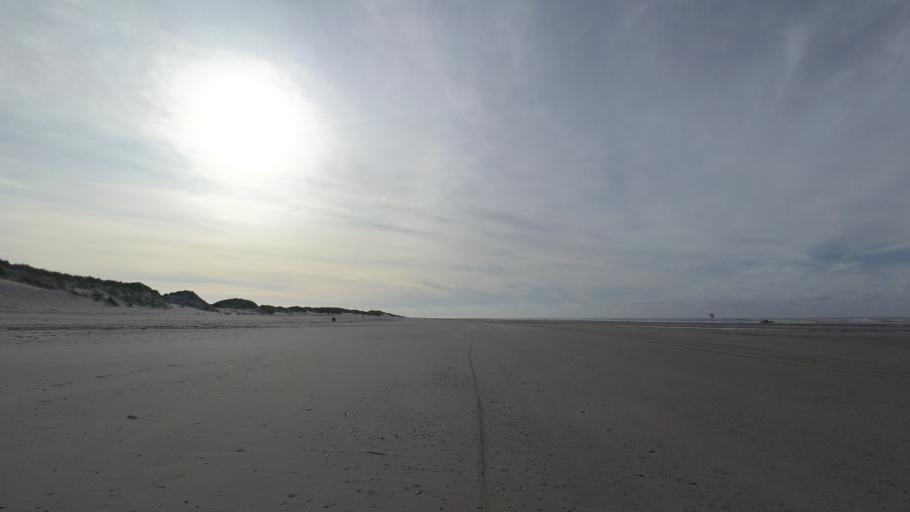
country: NL
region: Friesland
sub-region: Gemeente Dongeradeel
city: Holwerd
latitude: 53.4676
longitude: 5.9084
